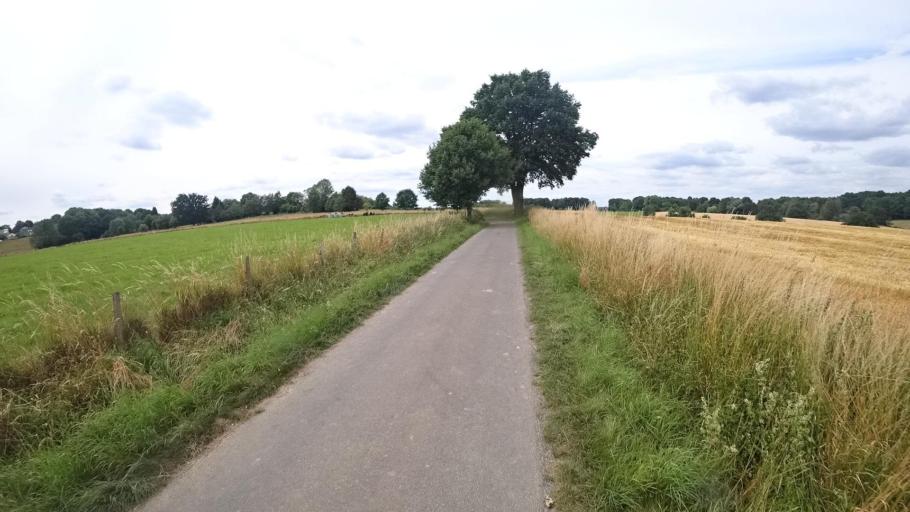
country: DE
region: Rheinland-Pfalz
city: Ziegenhain
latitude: 50.6774
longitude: 7.5331
